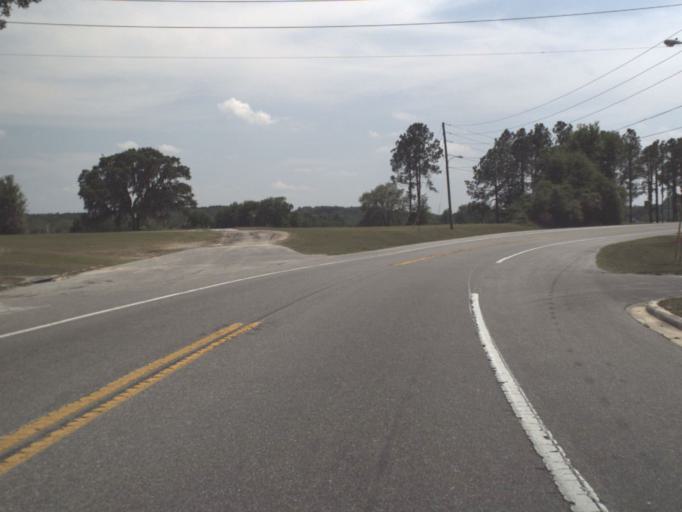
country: US
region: Florida
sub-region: Lake County
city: Howie In The Hills
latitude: 28.7083
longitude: -81.7710
